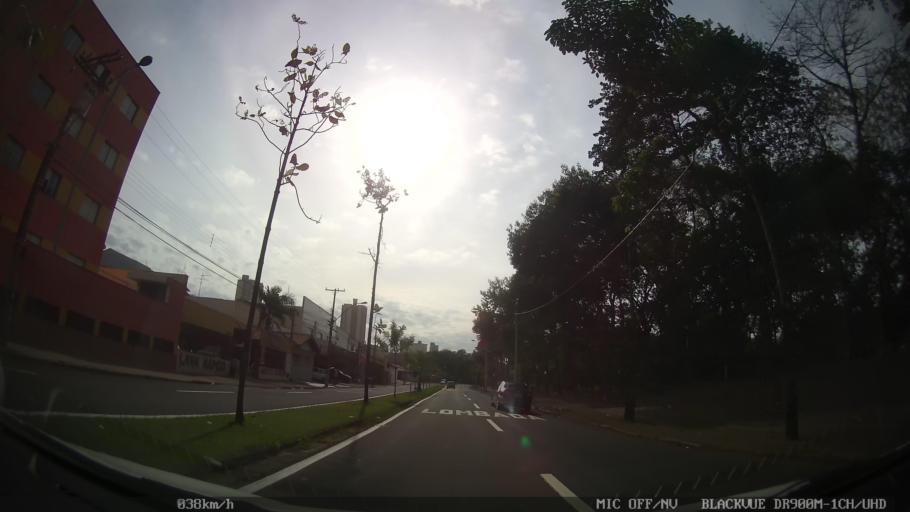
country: BR
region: Sao Paulo
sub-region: Piracicaba
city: Piracicaba
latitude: -22.7412
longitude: -47.6310
